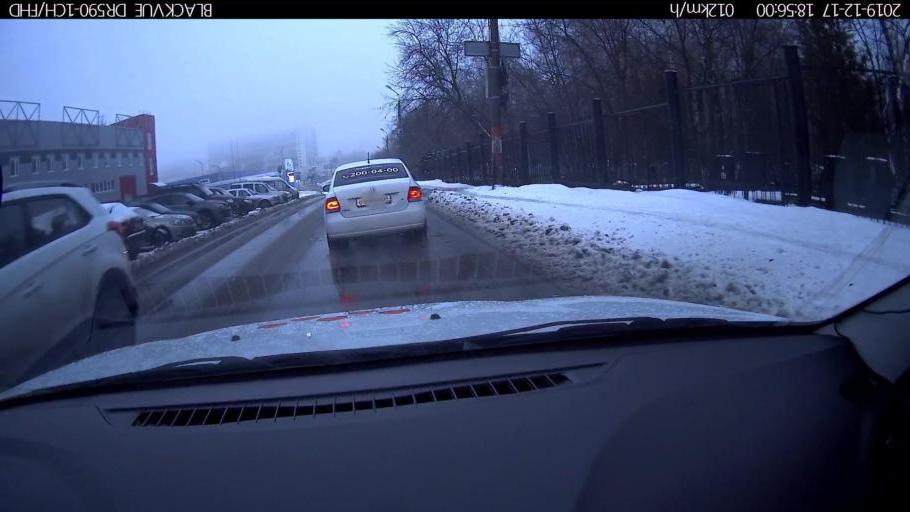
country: RU
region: Nizjnij Novgorod
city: Nizhniy Novgorod
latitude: 56.2846
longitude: 43.9987
